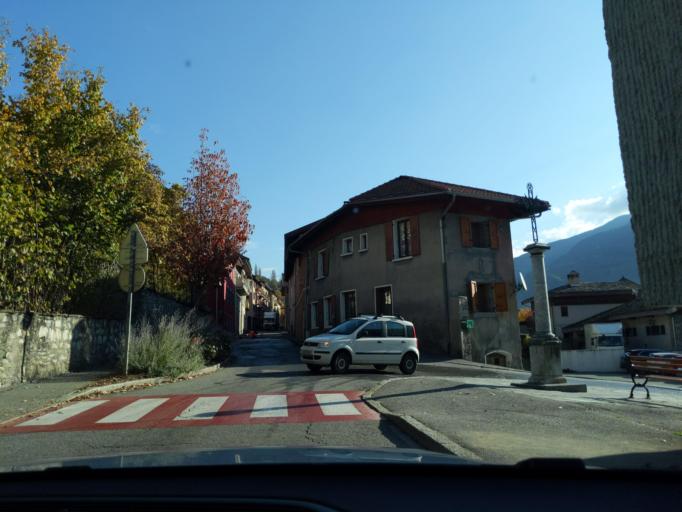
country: FR
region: Rhone-Alpes
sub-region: Departement de la Savoie
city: Aime
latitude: 45.5566
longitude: 6.6491
